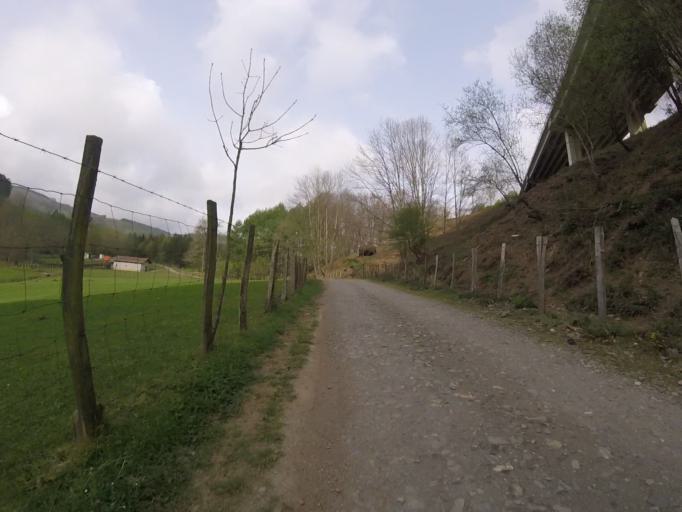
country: ES
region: Navarre
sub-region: Provincia de Navarra
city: Areso
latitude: 43.1073
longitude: -1.9530
